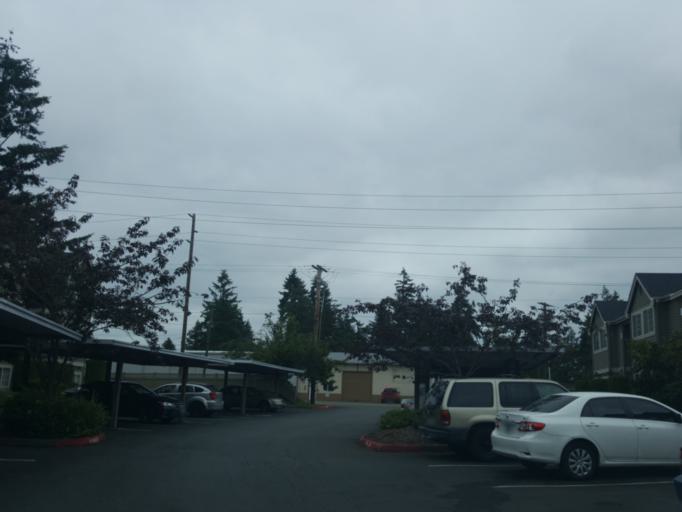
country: US
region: Washington
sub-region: Pierce County
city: Lakewood
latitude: 47.1607
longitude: -122.4961
